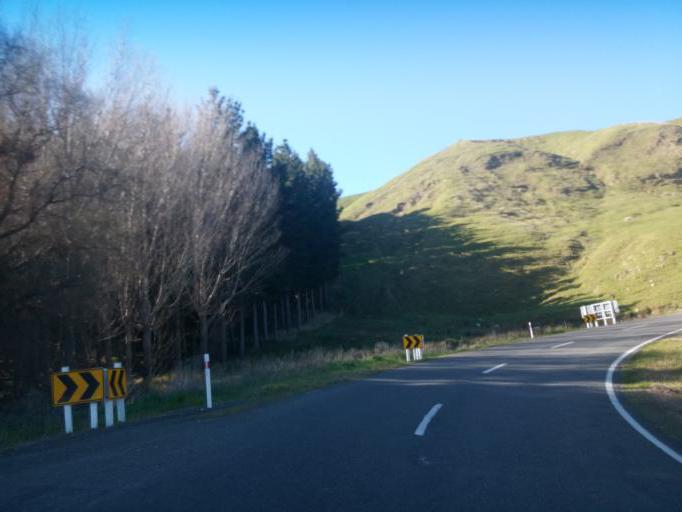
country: NZ
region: Wellington
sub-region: South Wairarapa District
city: Waipawa
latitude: -41.2940
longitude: 175.4812
